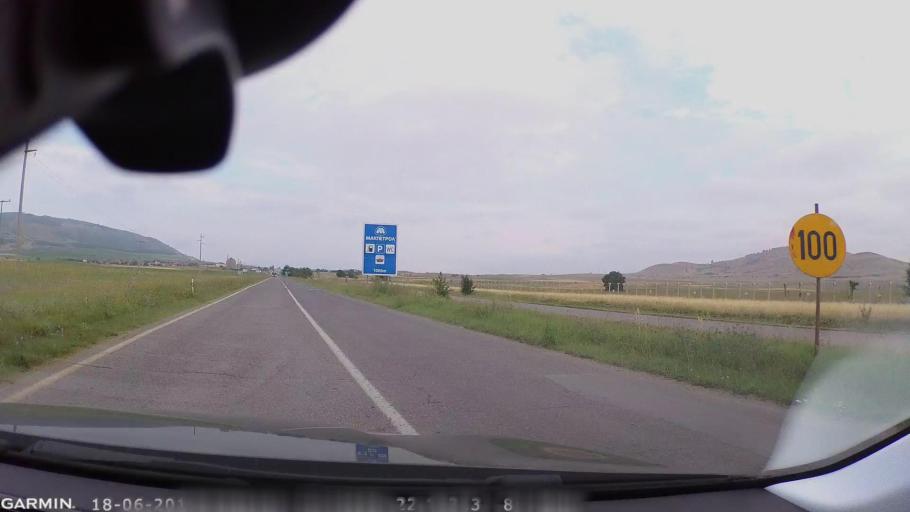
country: MK
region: Stip
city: Shtip
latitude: 41.7672
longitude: 22.1537
